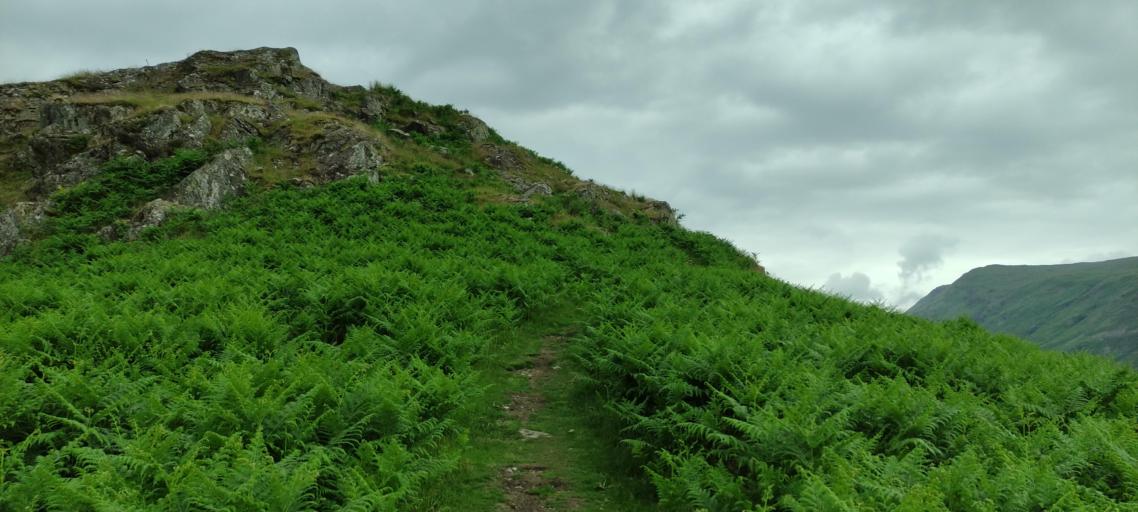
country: GB
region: England
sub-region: Cumbria
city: Ambleside
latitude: 54.5592
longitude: -2.8825
